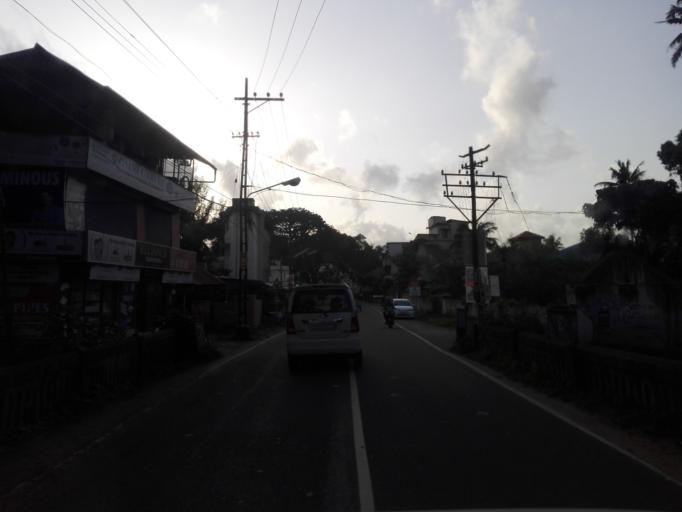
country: IN
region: Kerala
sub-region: Kottayam
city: Kottayam
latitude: 9.5957
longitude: 76.5131
